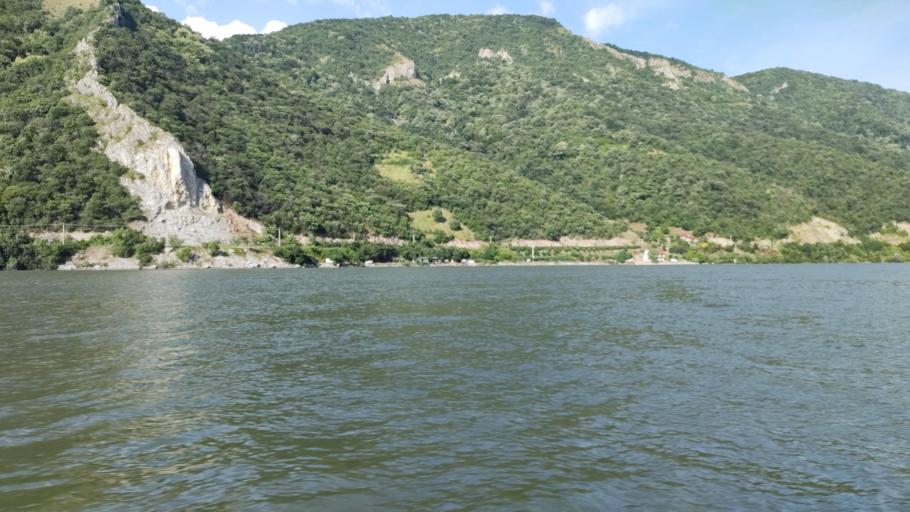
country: RO
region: Caras-Severin
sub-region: Comuna Berzasca
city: Berzasca
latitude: 44.5979
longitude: 22.0193
